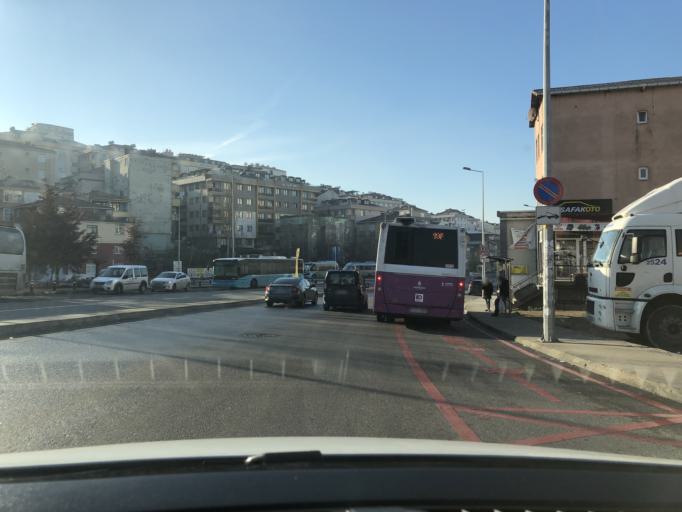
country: TR
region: Istanbul
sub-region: Atasehir
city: Atasehir
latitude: 40.9684
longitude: 29.1224
